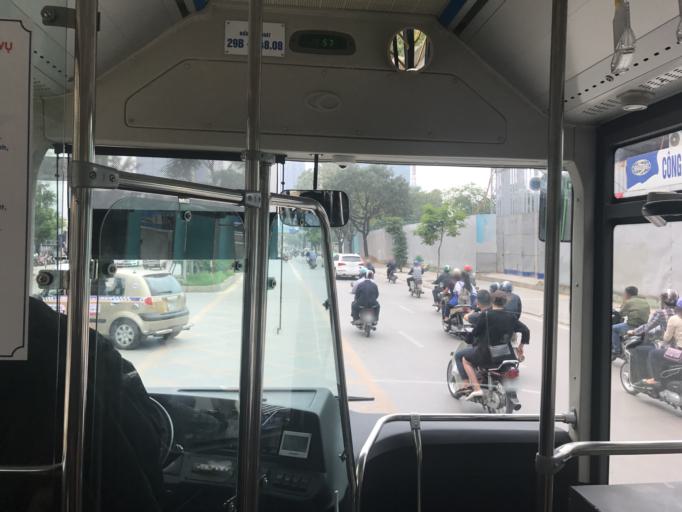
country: VN
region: Ha Noi
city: Dong Da
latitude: 21.0192
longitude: 105.8169
